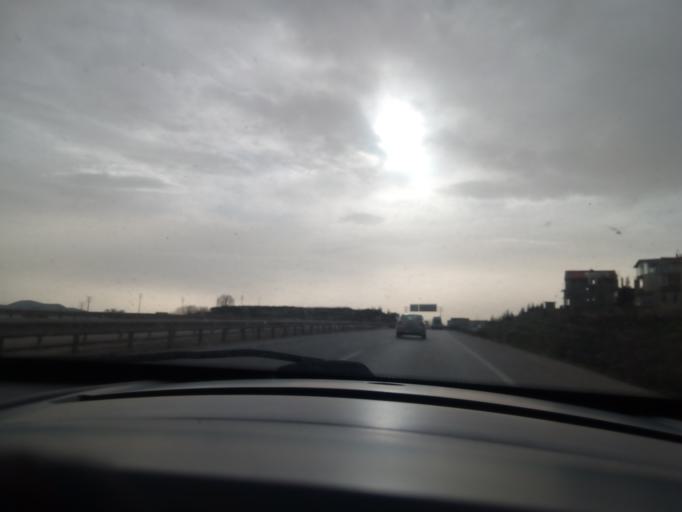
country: TR
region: Bursa
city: Tatkavakli
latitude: 40.0476
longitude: 28.3748
